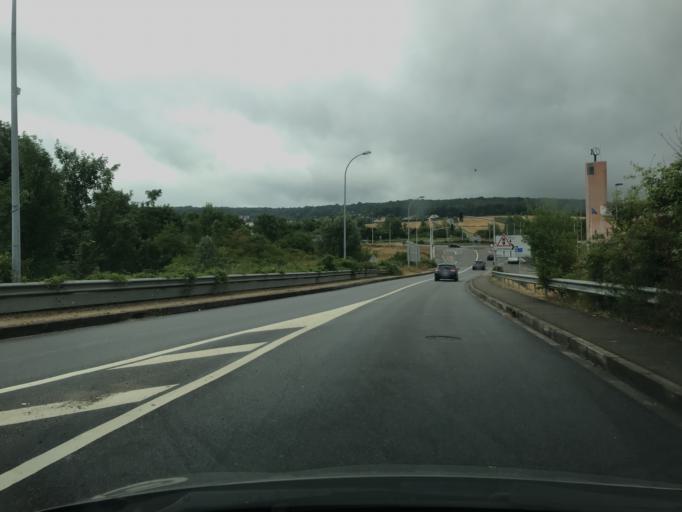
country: FR
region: Ile-de-France
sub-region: Departement des Yvelines
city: Chambourcy
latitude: 48.9158
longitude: 2.0239
